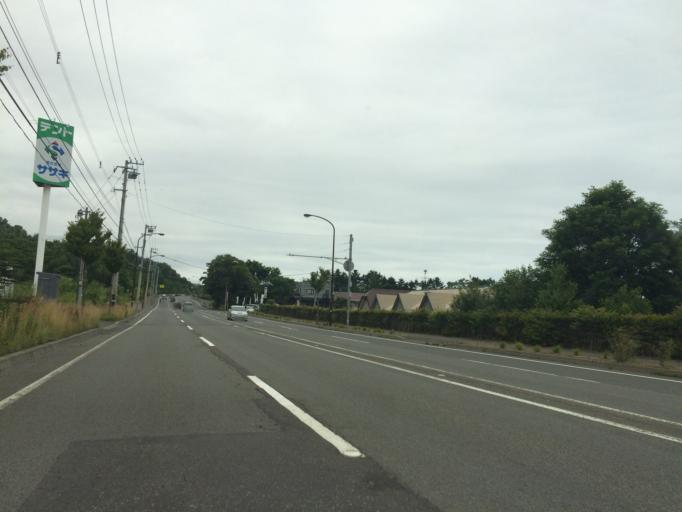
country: JP
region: Hokkaido
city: Otaru
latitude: 43.1448
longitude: 141.1431
